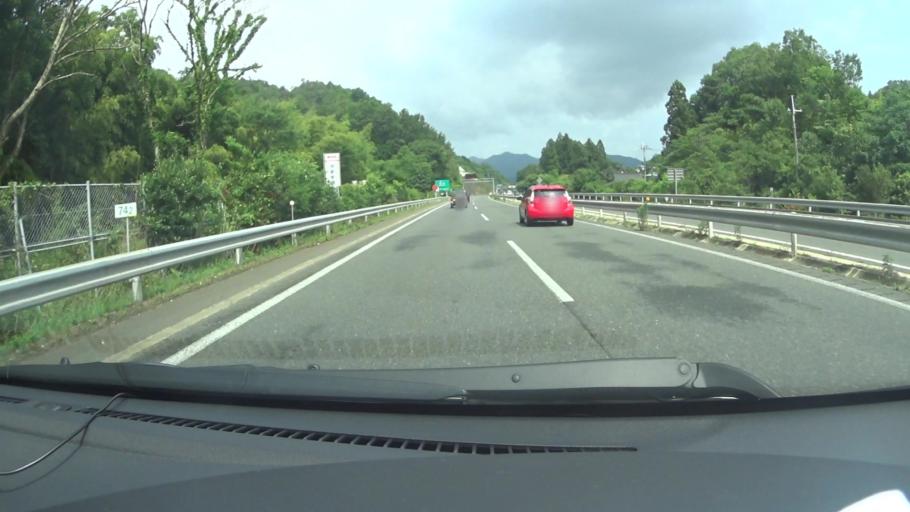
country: JP
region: Kyoto
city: Kameoka
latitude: 35.0022
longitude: 135.5697
